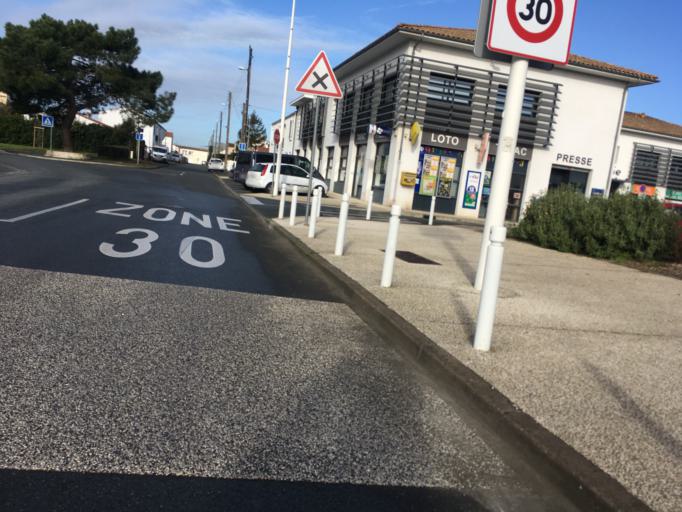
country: FR
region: Poitou-Charentes
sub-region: Departement de la Charente-Maritime
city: La Rochelle
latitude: 46.1717
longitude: -1.1799
